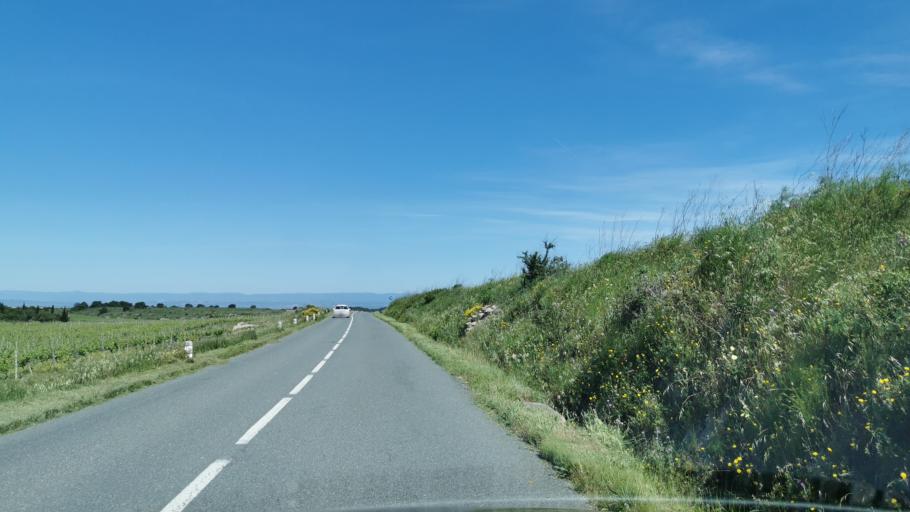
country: FR
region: Languedoc-Roussillon
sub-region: Departement de l'Aude
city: Armissan
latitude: 43.1713
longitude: 3.1134
